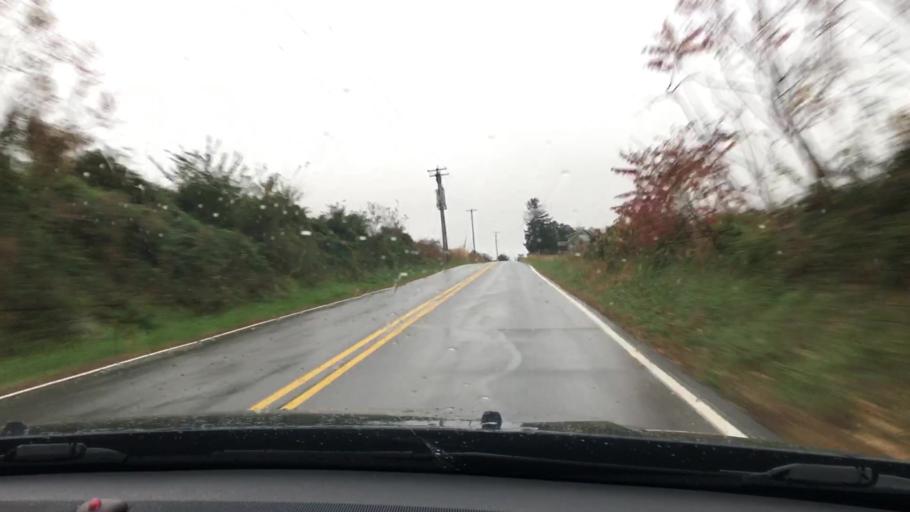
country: US
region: Pennsylvania
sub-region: York County
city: Stewartstown
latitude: 39.7473
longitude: -76.4868
